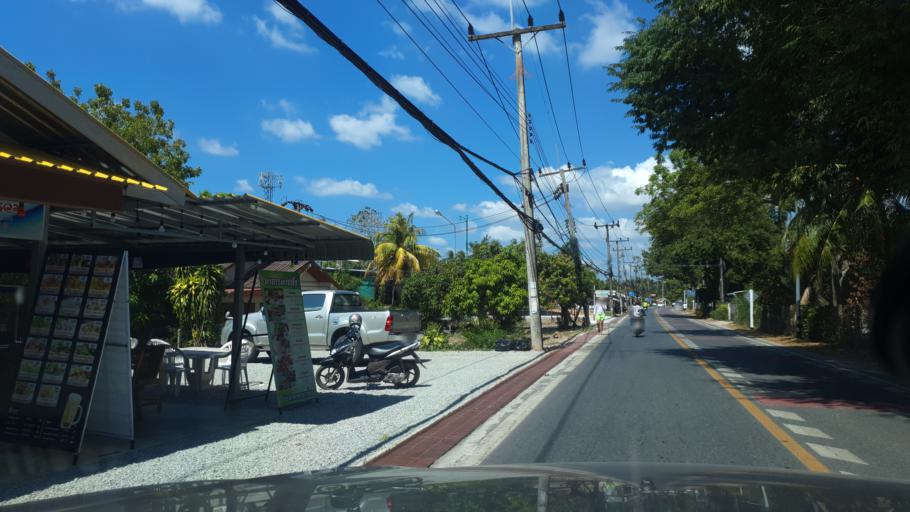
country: TH
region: Phuket
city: Thalang
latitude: 8.1235
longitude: 98.3082
